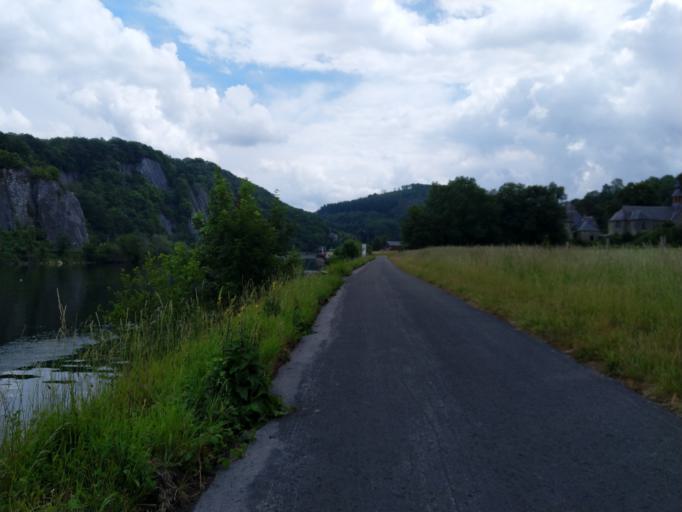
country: BE
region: Wallonia
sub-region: Province de Namur
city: Yvoir
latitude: 50.3379
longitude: 4.8648
